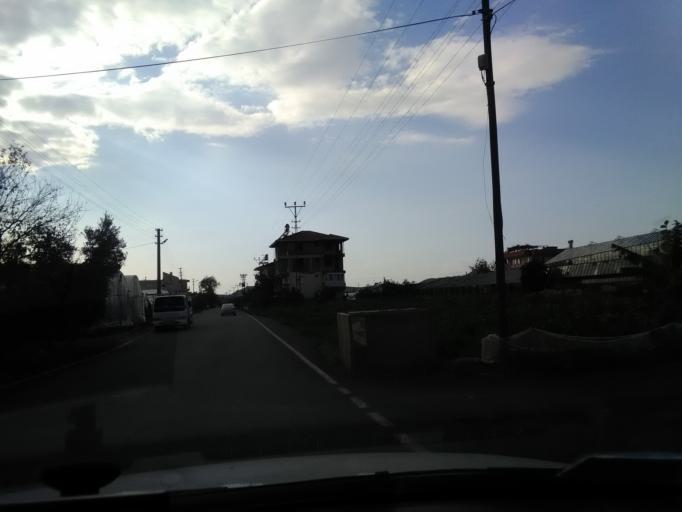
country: TR
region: Antalya
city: Gazipasa
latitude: 36.2733
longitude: 32.3381
